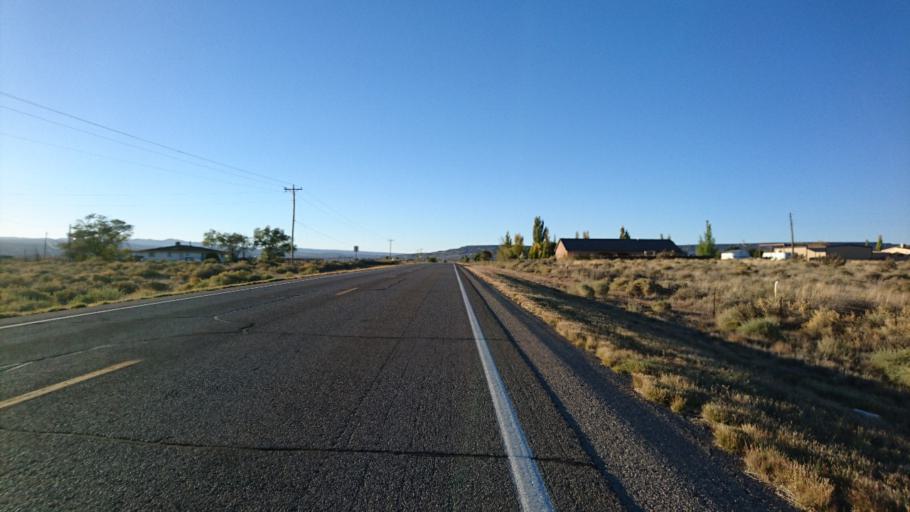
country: US
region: New Mexico
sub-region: Cibola County
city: Grants
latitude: 35.1263
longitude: -107.8037
